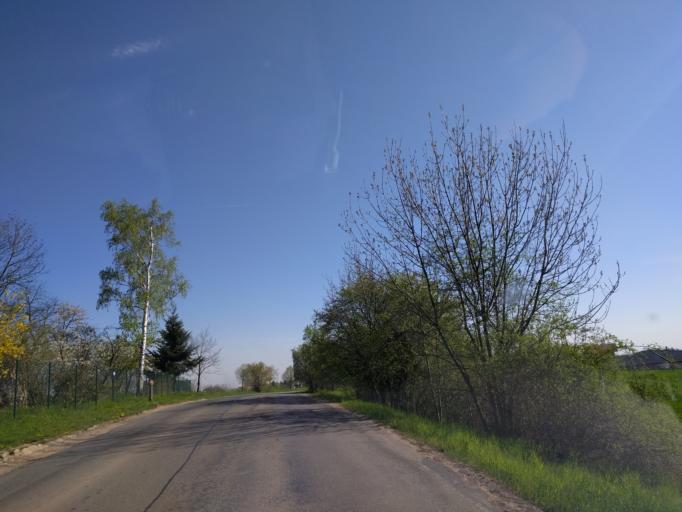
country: CZ
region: Central Bohemia
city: Mukarov
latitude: 50.0133
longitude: 14.7810
